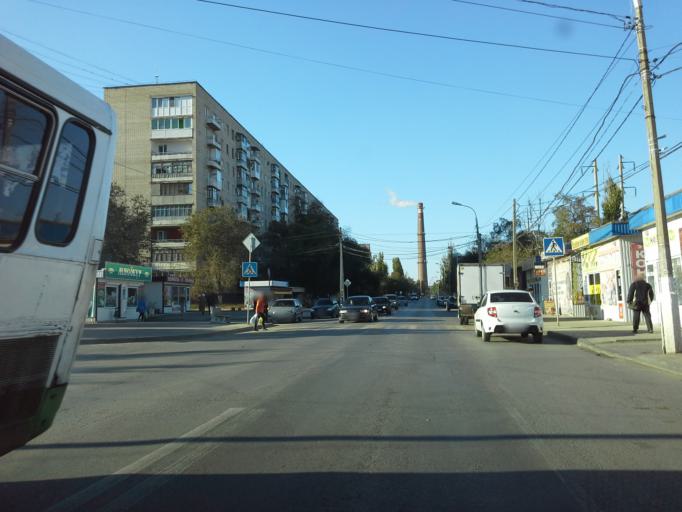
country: RU
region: Volgograd
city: Vodstroy
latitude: 48.8208
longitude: 44.6325
